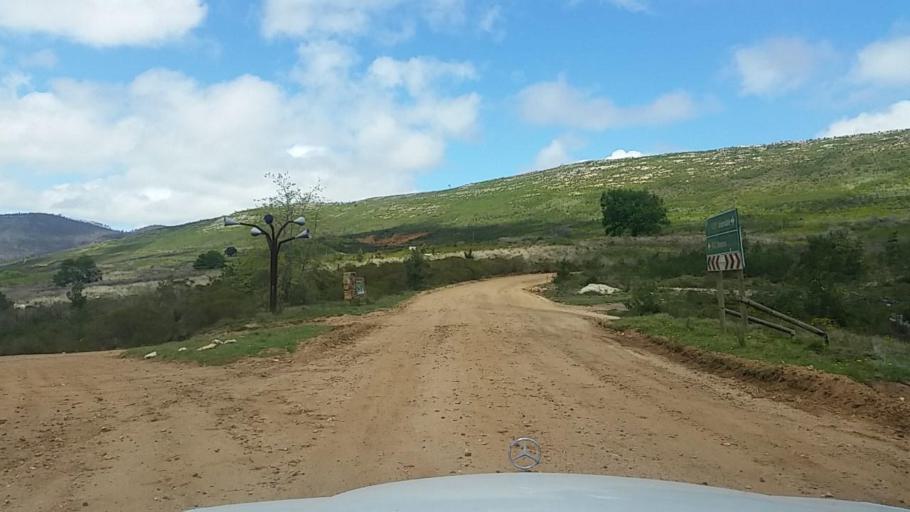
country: ZA
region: Western Cape
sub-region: Eden District Municipality
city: Knysna
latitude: -33.8825
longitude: 23.1582
